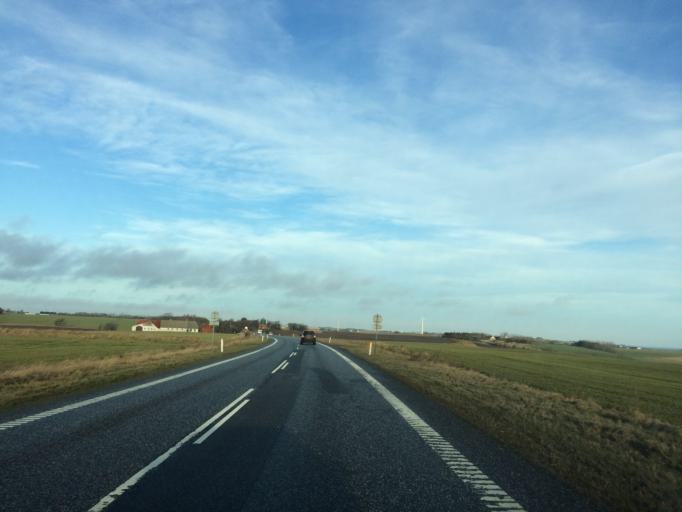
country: DK
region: North Denmark
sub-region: Thisted Kommune
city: Thisted
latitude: 56.8756
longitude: 8.5896
